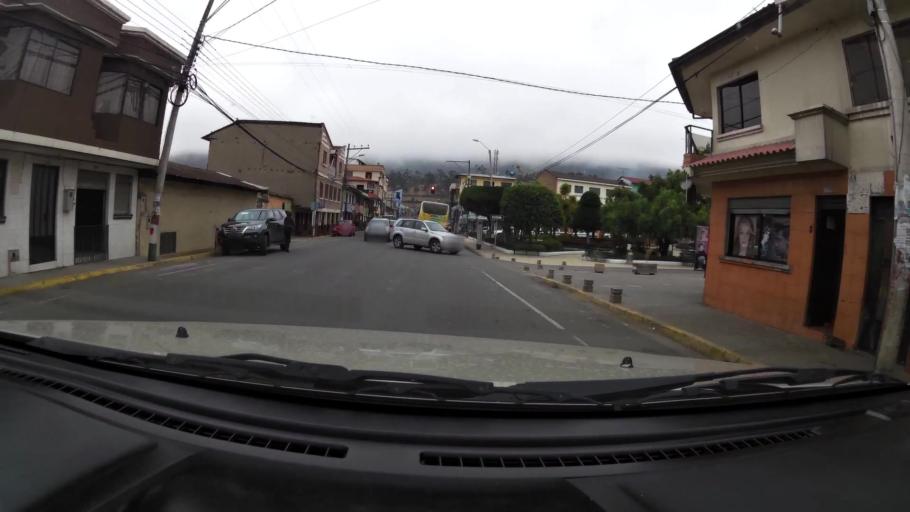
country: EC
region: Canar
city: Canar
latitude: -2.5110
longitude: -78.9289
